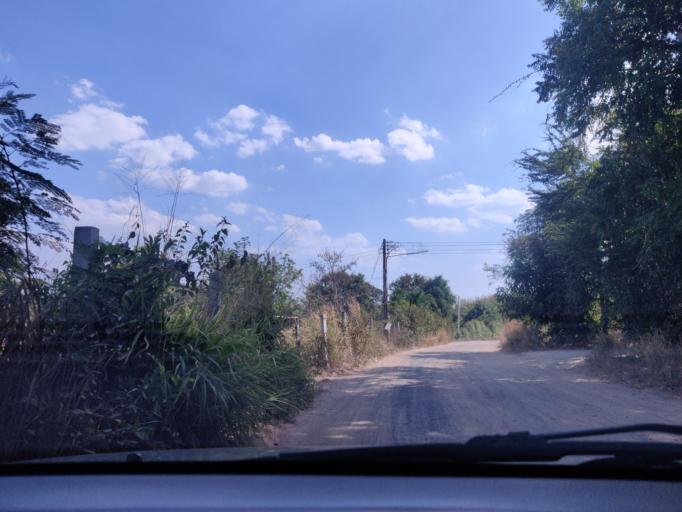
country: TH
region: Sisaket
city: Si Sa Ket
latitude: 15.0807
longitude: 104.3506
